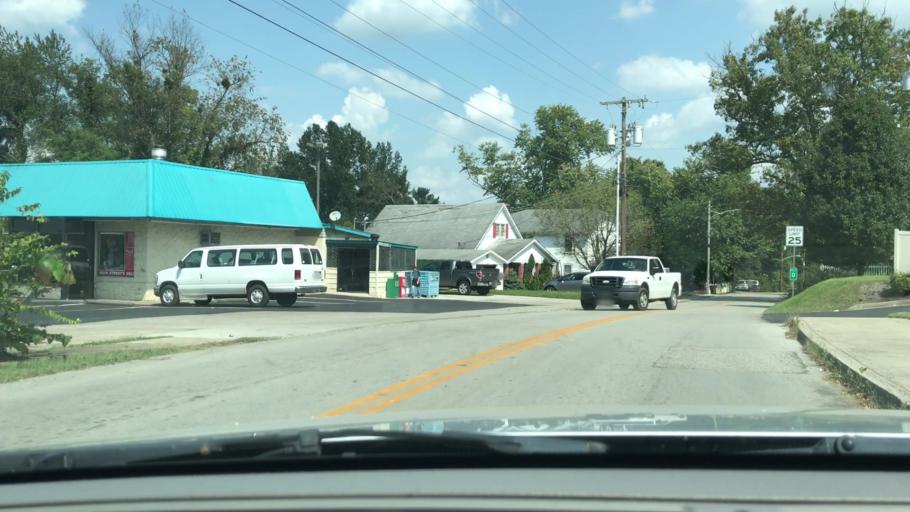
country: US
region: Kentucky
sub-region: Pulaski County
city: Somerset
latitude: 37.0997
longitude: -84.6073
